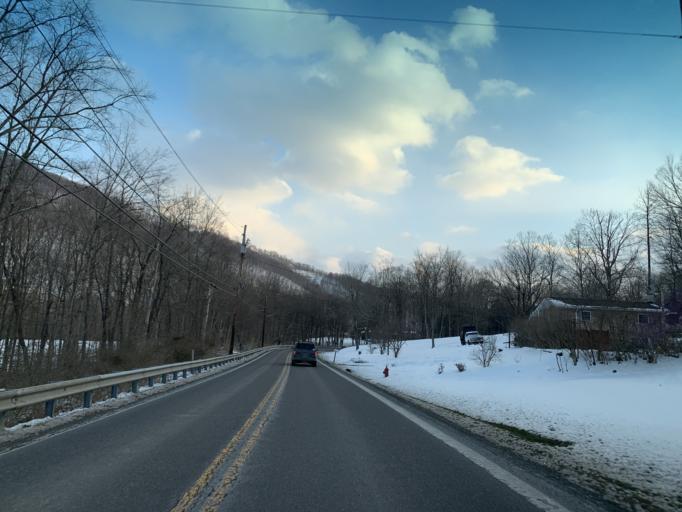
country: US
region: Maryland
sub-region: Allegany County
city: Cumberland
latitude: 39.7092
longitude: -78.7816
